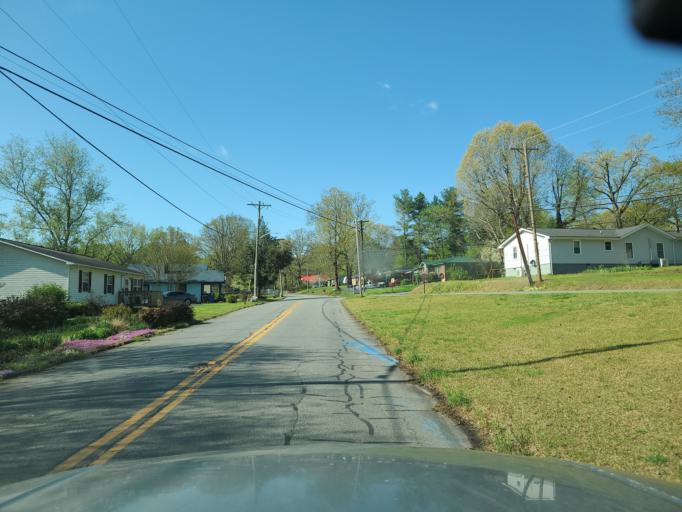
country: US
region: North Carolina
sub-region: Rutherford County
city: Spindale
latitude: 35.3719
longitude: -81.9256
